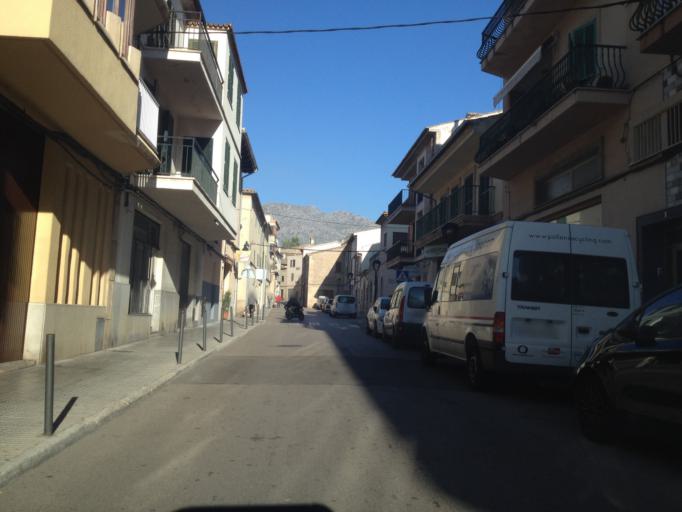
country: ES
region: Balearic Islands
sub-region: Illes Balears
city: Pollenca
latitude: 39.8780
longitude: 3.0191
